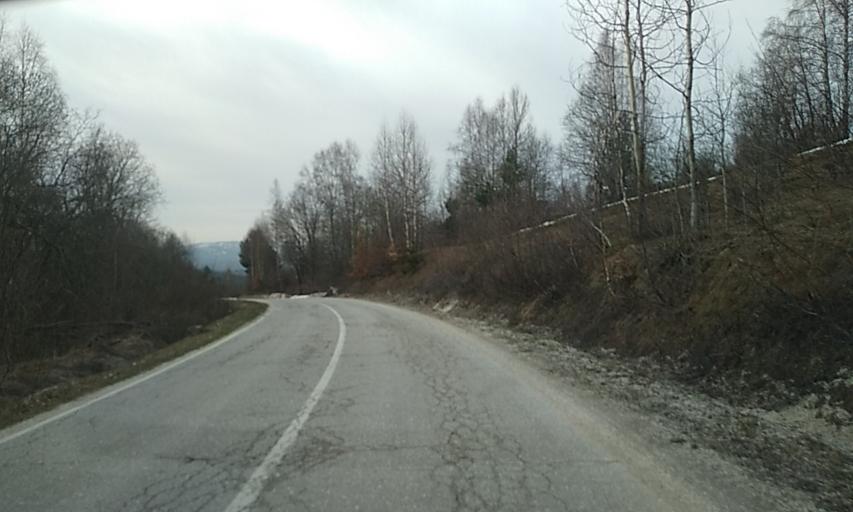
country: RS
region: Central Serbia
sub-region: Jablanicki Okrug
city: Crna Trava
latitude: 42.6739
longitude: 22.3750
